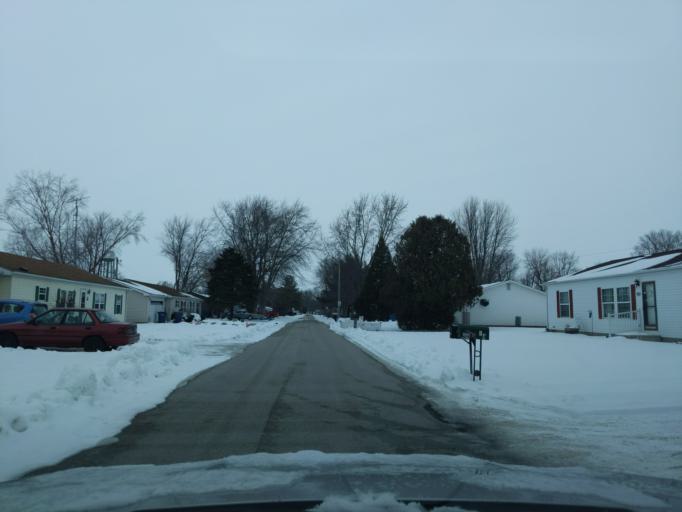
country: US
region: Indiana
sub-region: Benton County
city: Otterbein
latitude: 40.4818
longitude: -87.0917
